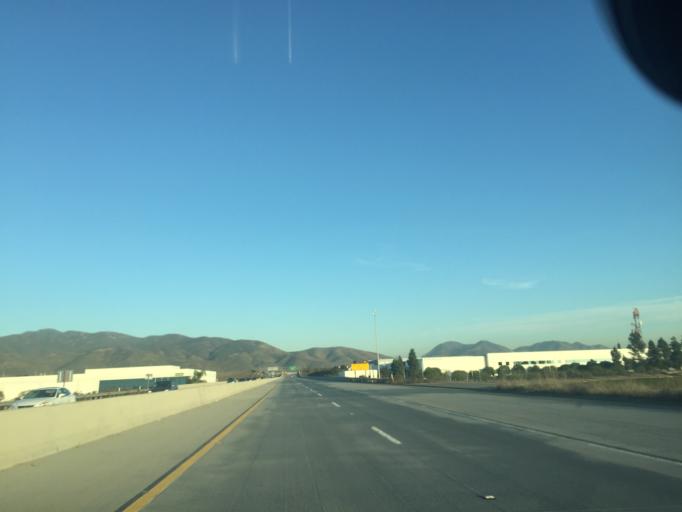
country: MX
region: Baja California
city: Tijuana
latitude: 32.5639
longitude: -116.9427
